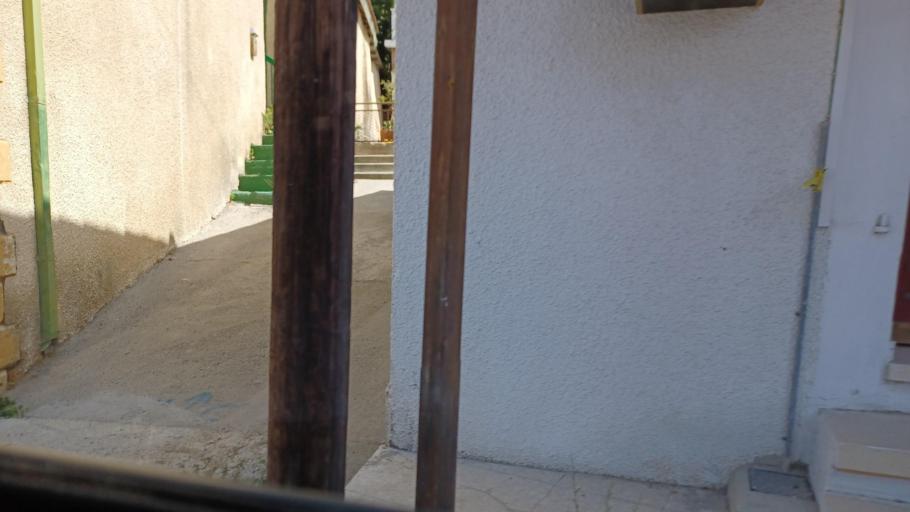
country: CY
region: Lefkosia
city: Kakopetria
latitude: 35.0401
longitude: 32.9006
